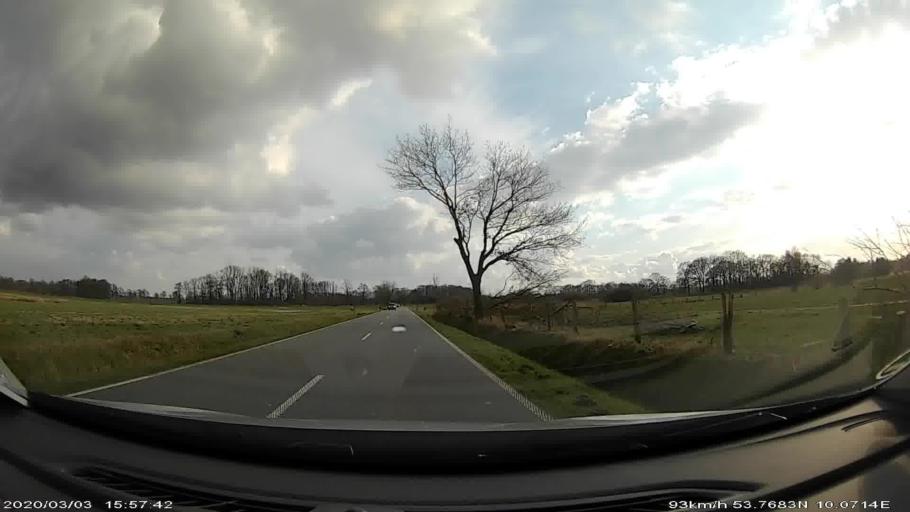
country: DE
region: Schleswig-Holstein
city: Tangstedt
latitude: 53.7701
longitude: 10.0715
